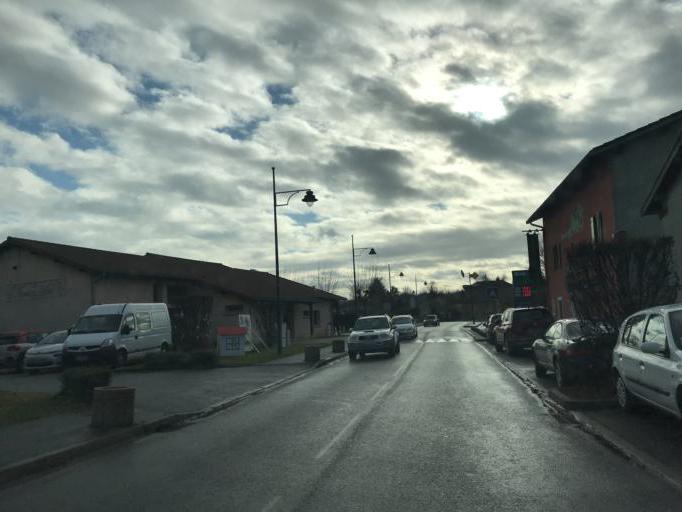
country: FR
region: Rhone-Alpes
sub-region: Departement de l'Ain
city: Sainte-Euphemie
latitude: 45.9723
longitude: 4.7993
